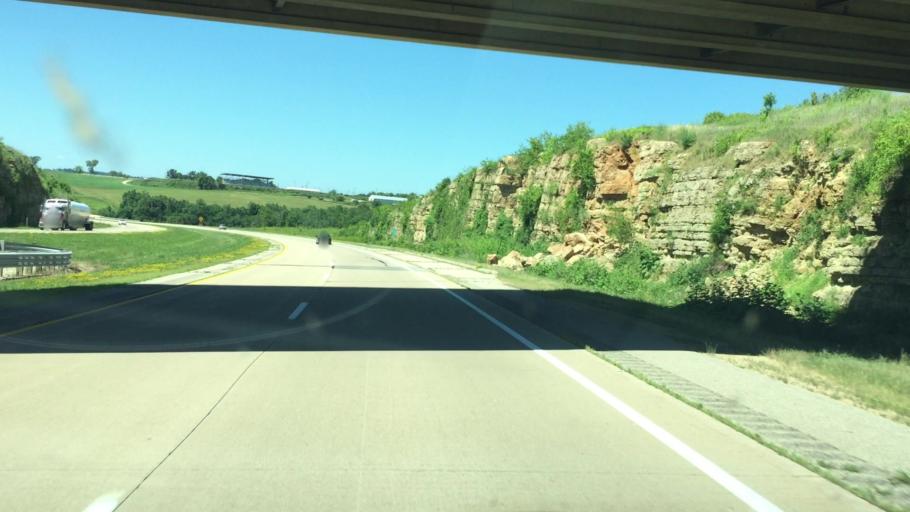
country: US
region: Wisconsin
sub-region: Iowa County
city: Mineral Point
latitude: 42.8483
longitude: -90.1983
